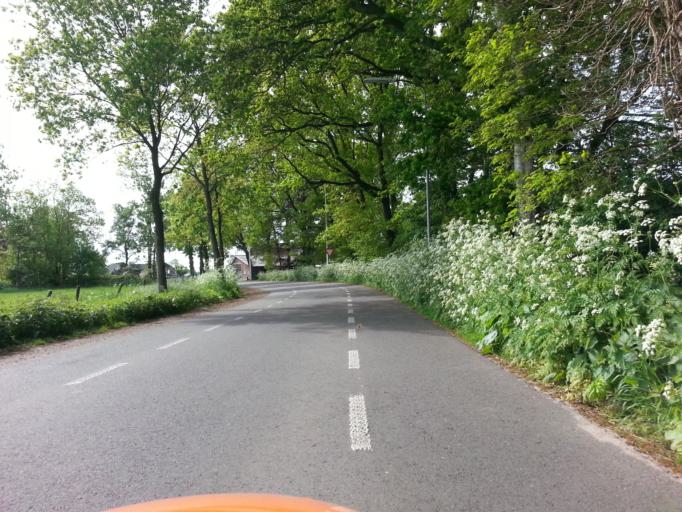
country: NL
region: Gelderland
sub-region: Gemeente Barneveld
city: Barneveld
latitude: 52.1143
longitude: 5.5531
